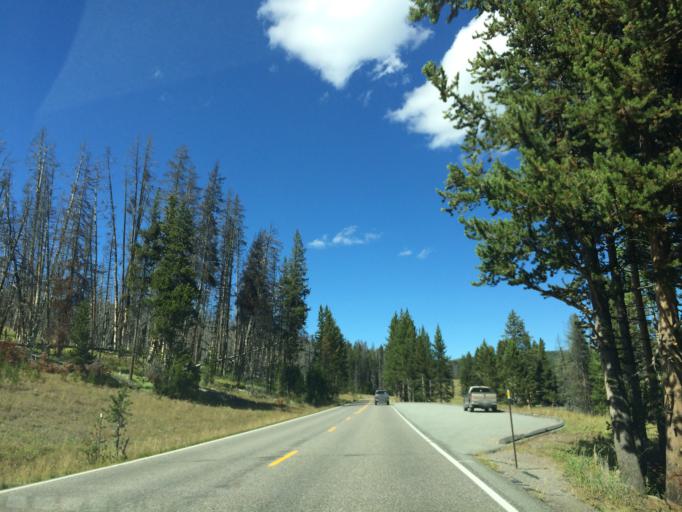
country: US
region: Montana
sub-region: Gallatin County
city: West Yellowstone
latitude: 44.5931
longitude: -110.3867
